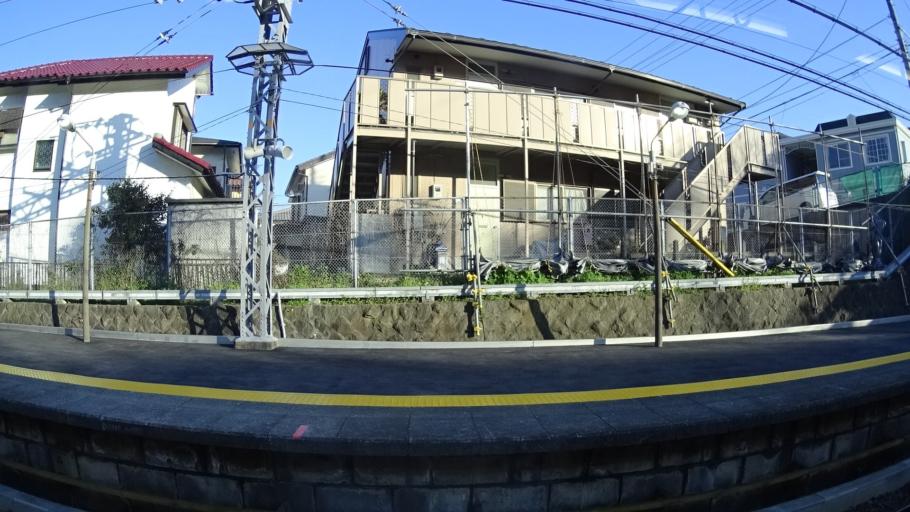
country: JP
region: Kanagawa
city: Miura
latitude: 35.1981
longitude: 139.6648
